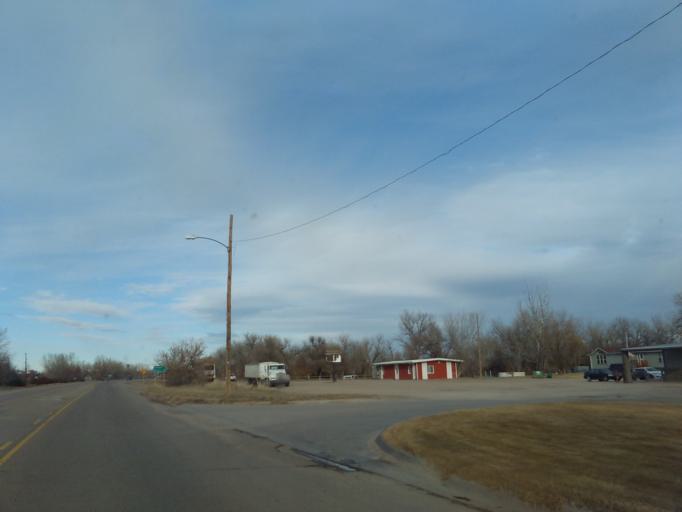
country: US
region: Nebraska
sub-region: Morrill County
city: Bridgeport
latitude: 41.6737
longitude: -103.0988
